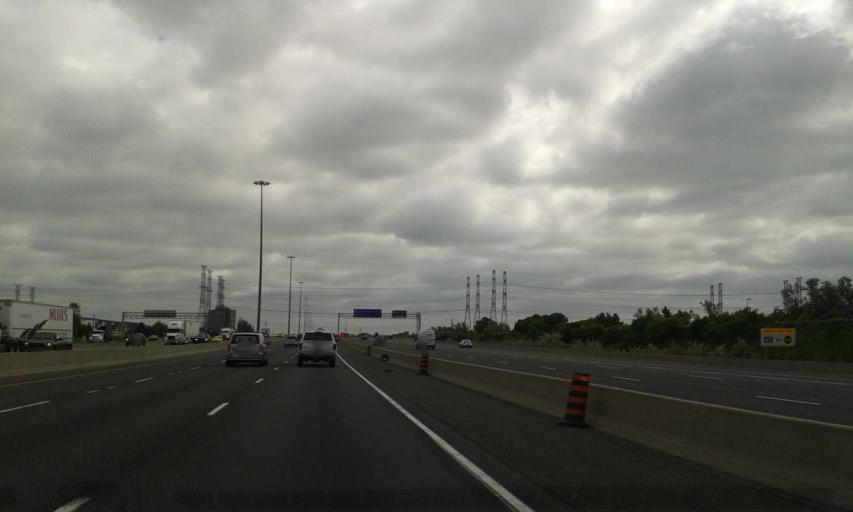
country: CA
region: Ontario
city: Ajax
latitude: 43.8333
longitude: -79.0826
